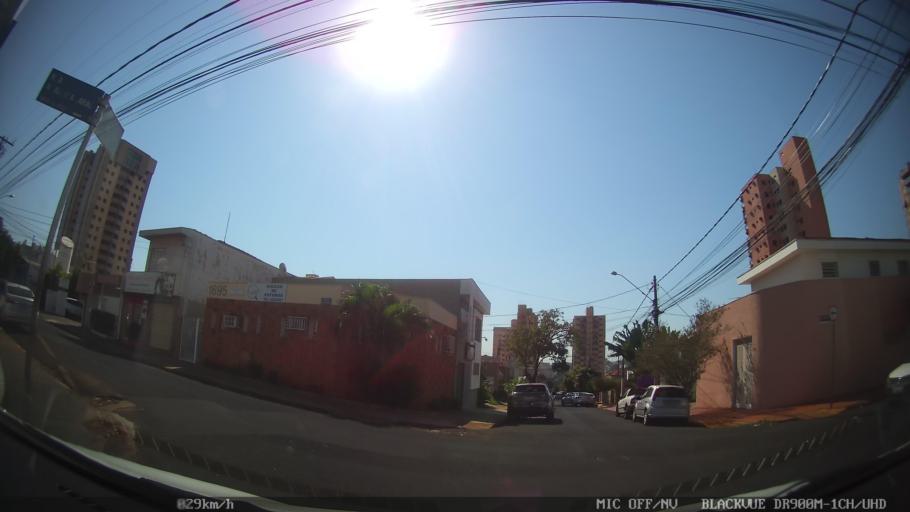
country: BR
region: Sao Paulo
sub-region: Ribeirao Preto
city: Ribeirao Preto
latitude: -21.1880
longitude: -47.8034
